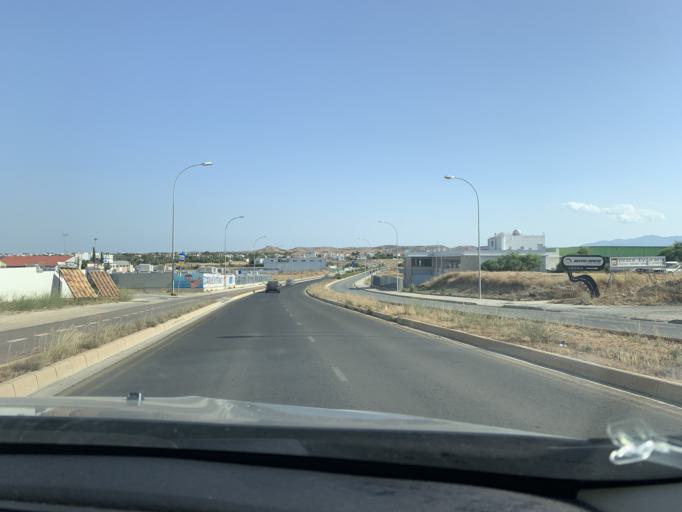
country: CY
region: Lefkosia
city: Nicosia
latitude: 35.1204
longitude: 33.3566
